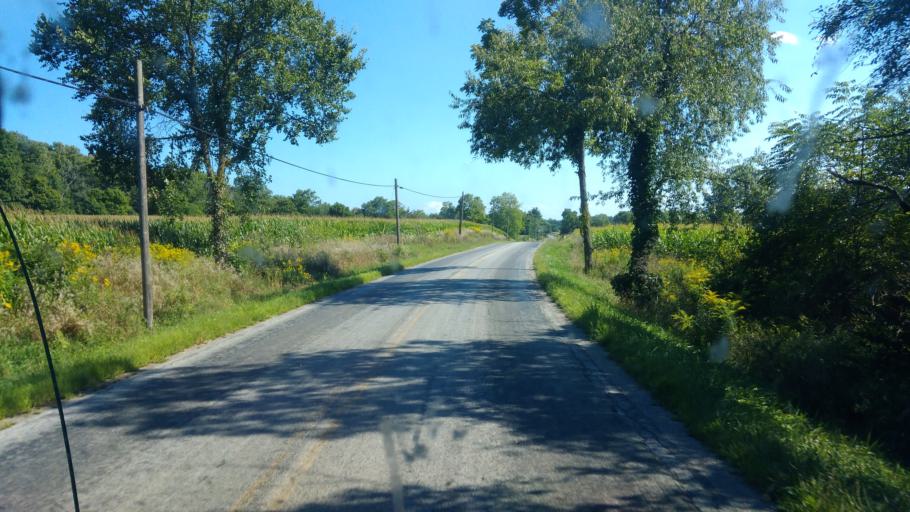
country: US
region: Ohio
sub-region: Ashland County
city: Ashland
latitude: 40.8947
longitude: -82.4299
